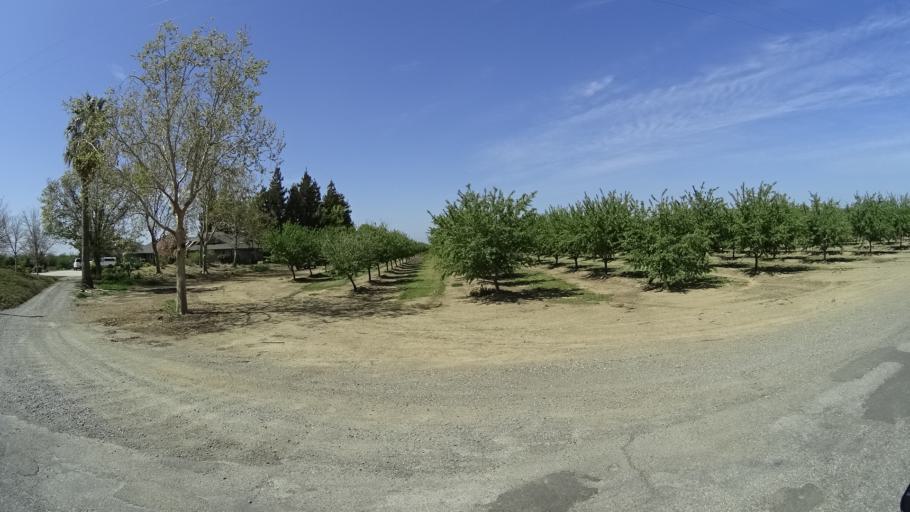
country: US
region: California
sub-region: Glenn County
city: Hamilton City
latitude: 39.6508
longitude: -122.0743
